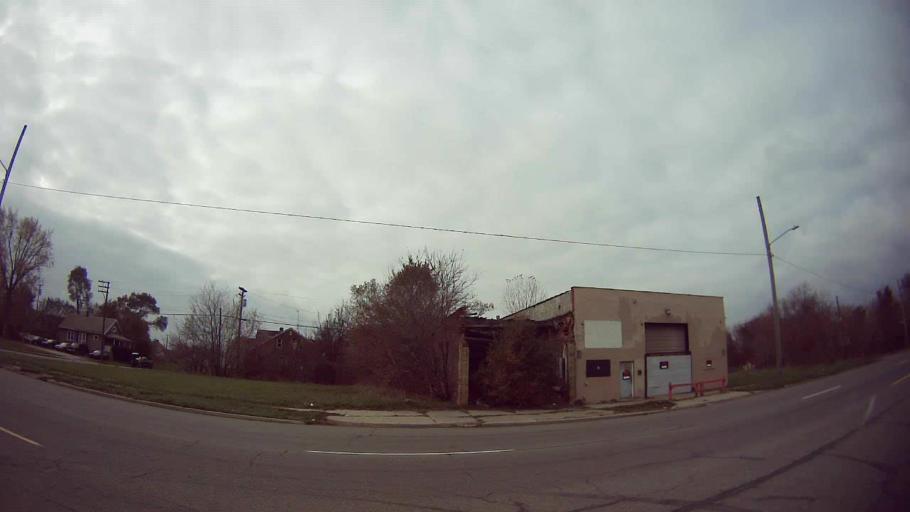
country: US
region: Michigan
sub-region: Wayne County
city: Hamtramck
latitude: 42.3991
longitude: -83.0229
